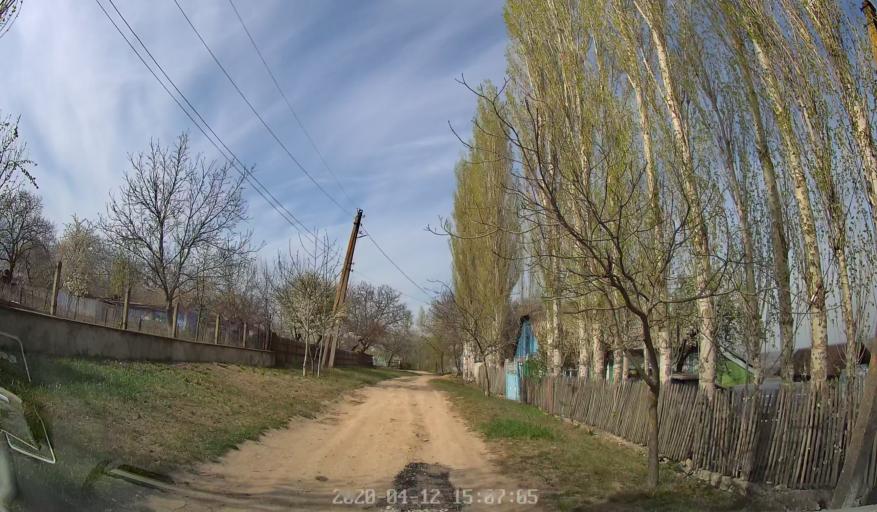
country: MD
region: Telenesti
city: Cocieri
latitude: 47.3156
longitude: 29.0724
